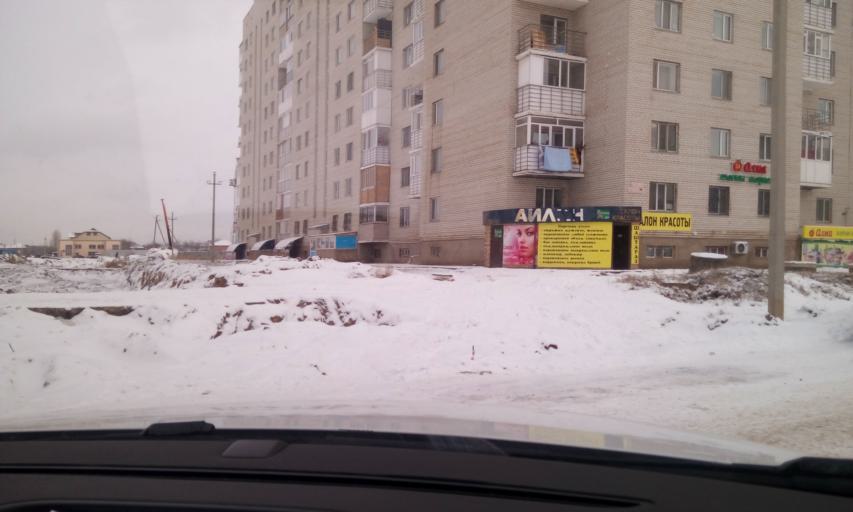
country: KZ
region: Astana Qalasy
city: Astana
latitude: 51.1281
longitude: 71.5034
